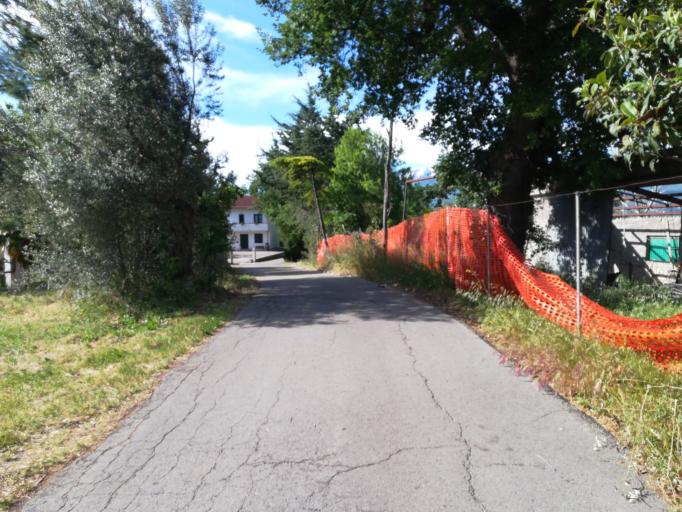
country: IT
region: Abruzzo
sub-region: Provincia di Chieti
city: Bucchianico
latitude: 42.2924
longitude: 14.1673
